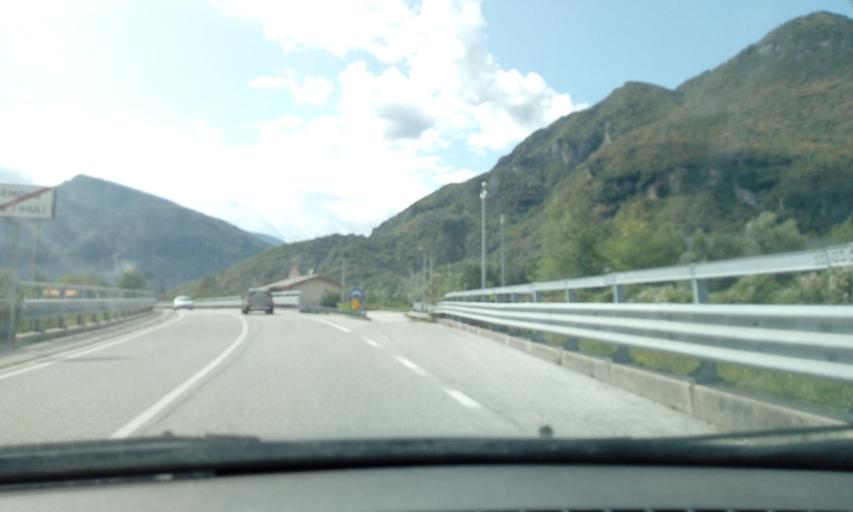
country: IT
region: Friuli Venezia Giulia
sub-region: Provincia di Udine
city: Gemona
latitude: 46.2824
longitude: 13.1000
